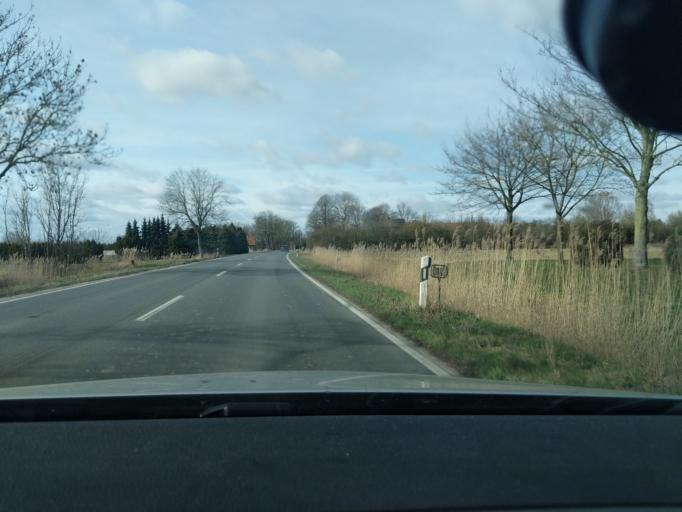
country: DE
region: Lower Saxony
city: Drochtersen
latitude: 53.6954
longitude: 9.4208
